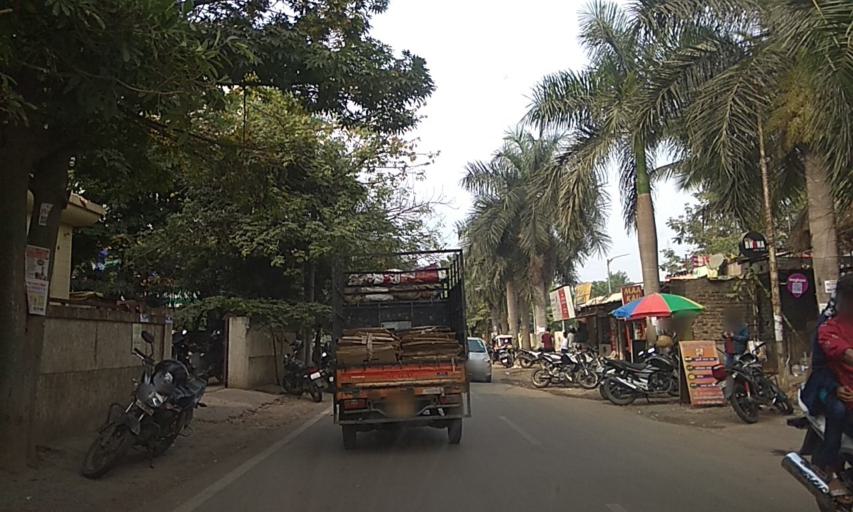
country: IN
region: Maharashtra
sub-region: Pune Division
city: Pune
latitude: 18.5042
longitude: 73.9312
